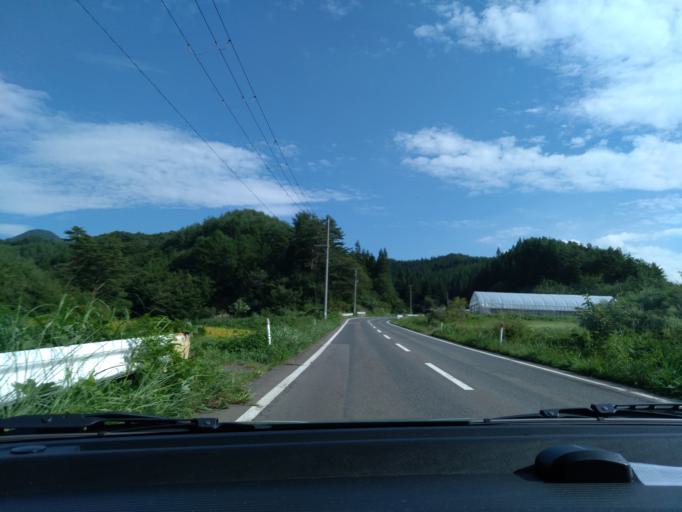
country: JP
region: Iwate
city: Shizukuishi
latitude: 39.6421
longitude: 141.0035
